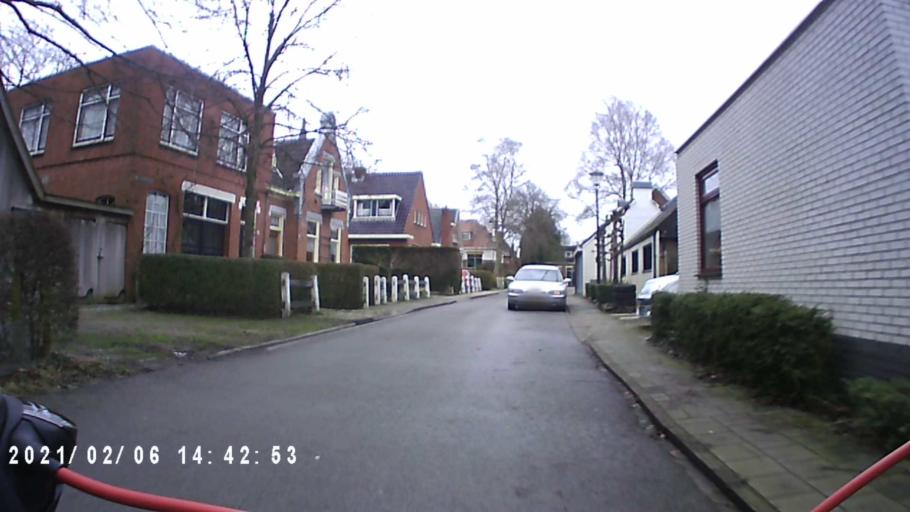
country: NL
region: Groningen
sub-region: Gemeente Winsum
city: Winsum
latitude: 53.3910
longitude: 6.5595
